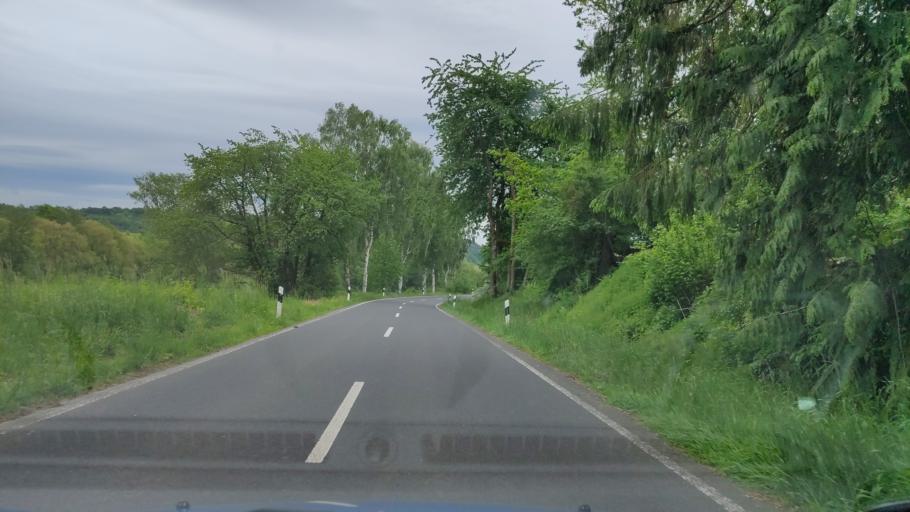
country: DE
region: Lower Saxony
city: Hardegsen
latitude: 51.6963
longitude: 9.7925
